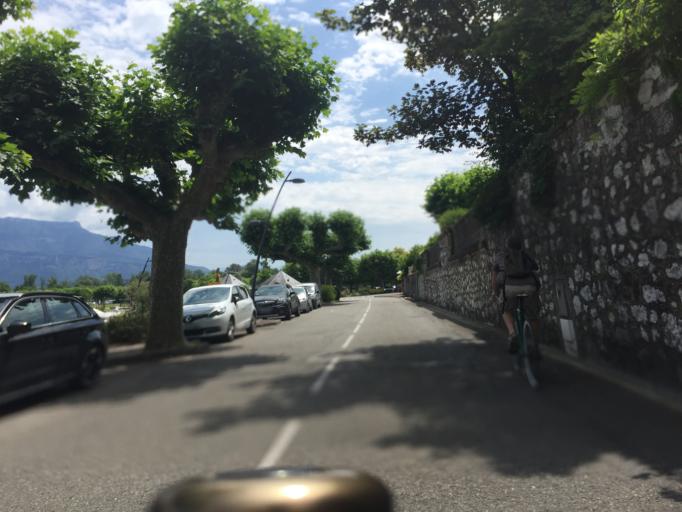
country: FR
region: Rhone-Alpes
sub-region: Departement de la Savoie
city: Le Bourget-du-Lac
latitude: 45.6566
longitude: 5.8588
